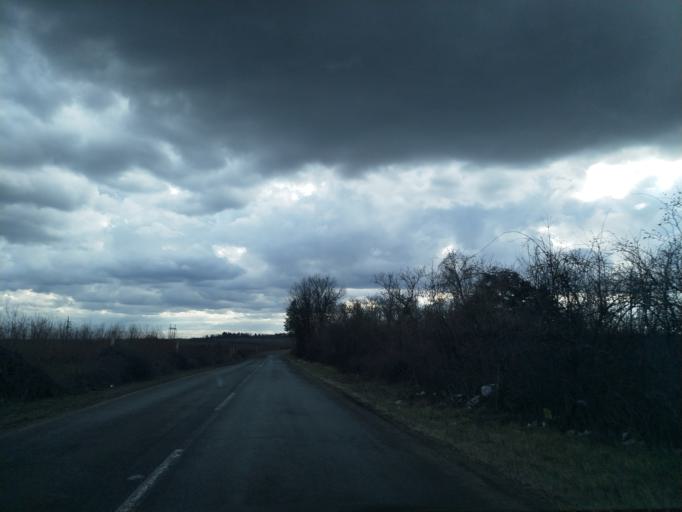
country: RS
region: Central Serbia
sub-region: Belgrade
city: Grocka
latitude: 44.6351
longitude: 20.7498
